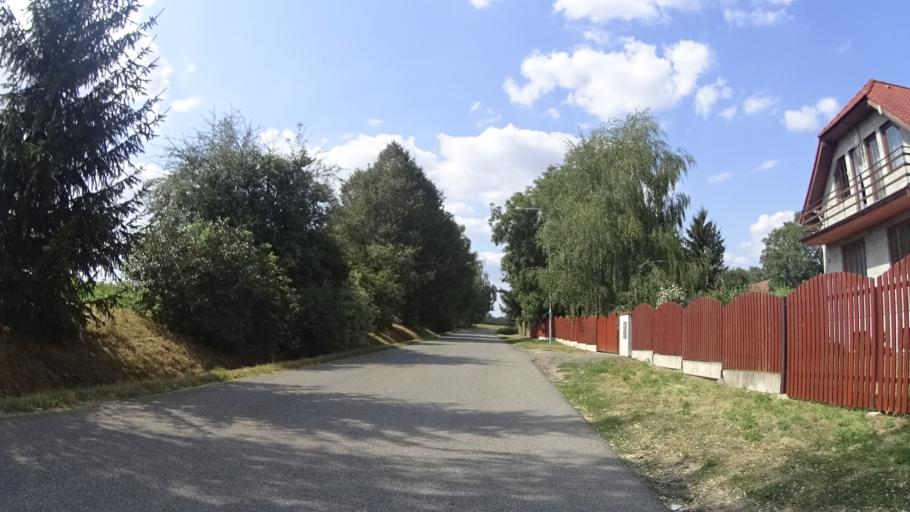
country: CZ
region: Kralovehradecky
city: Liban
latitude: 50.4082
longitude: 15.2666
